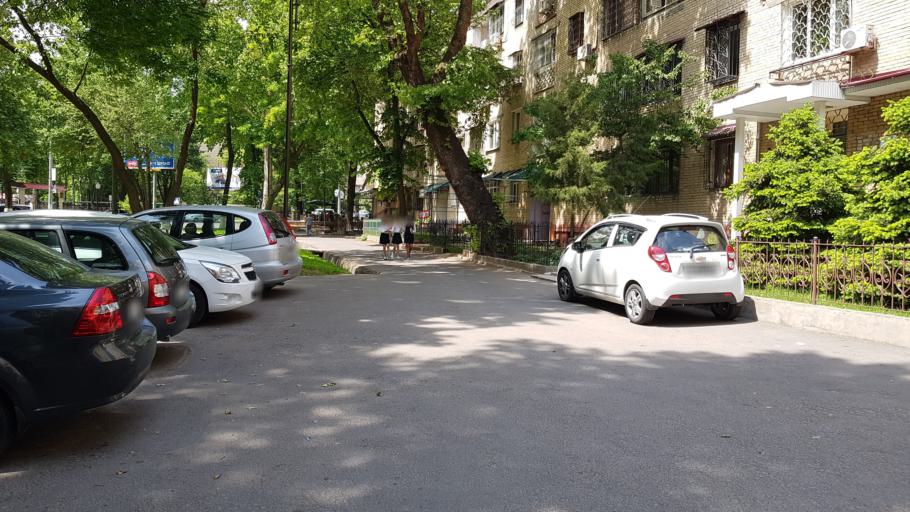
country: UZ
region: Toshkent Shahri
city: Tashkent
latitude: 41.3126
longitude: 69.2925
